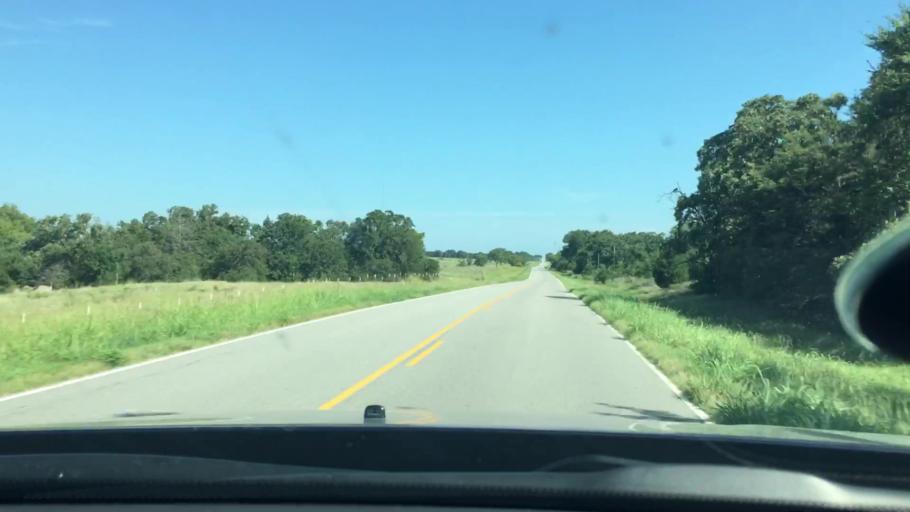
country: US
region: Oklahoma
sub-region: Johnston County
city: Tishomingo
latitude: 34.3117
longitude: -96.5488
